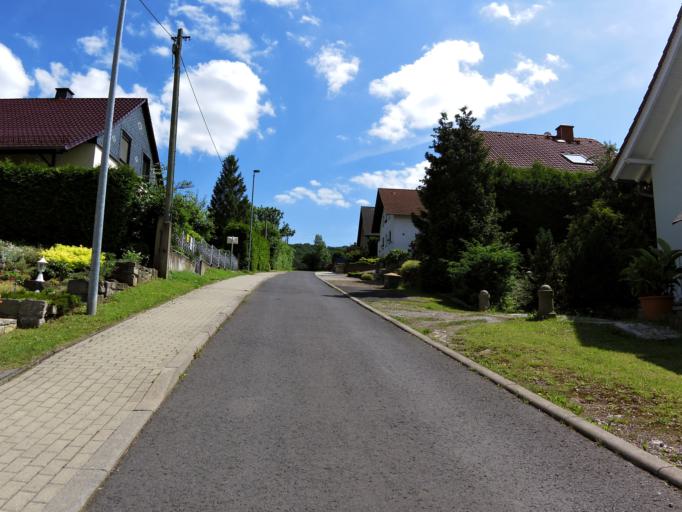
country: DE
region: Thuringia
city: Seebach
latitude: 50.9723
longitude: 10.4479
